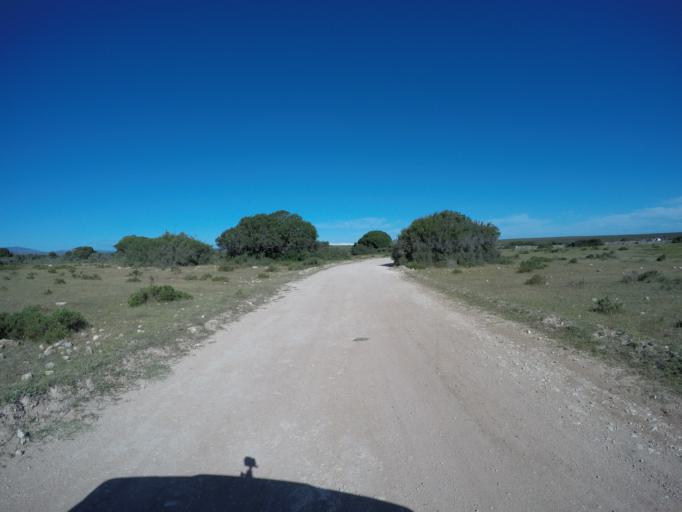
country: ZA
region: Western Cape
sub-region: Overberg District Municipality
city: Bredasdorp
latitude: -34.4528
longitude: 20.4082
